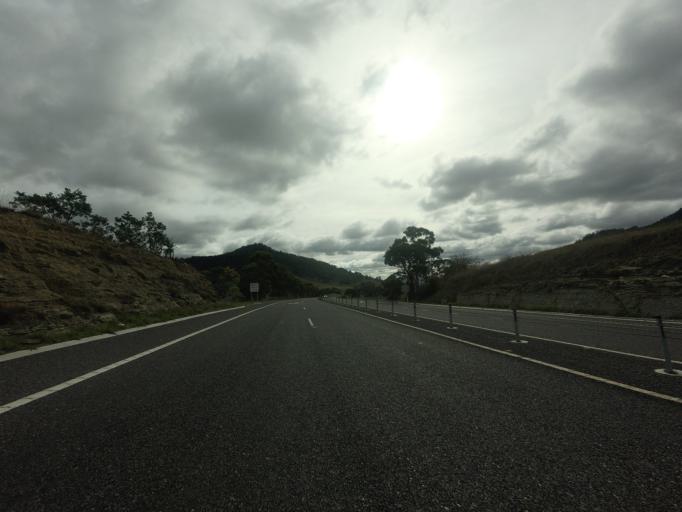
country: AU
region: Tasmania
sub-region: Brighton
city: Bridgewater
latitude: -42.5696
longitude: 147.2109
